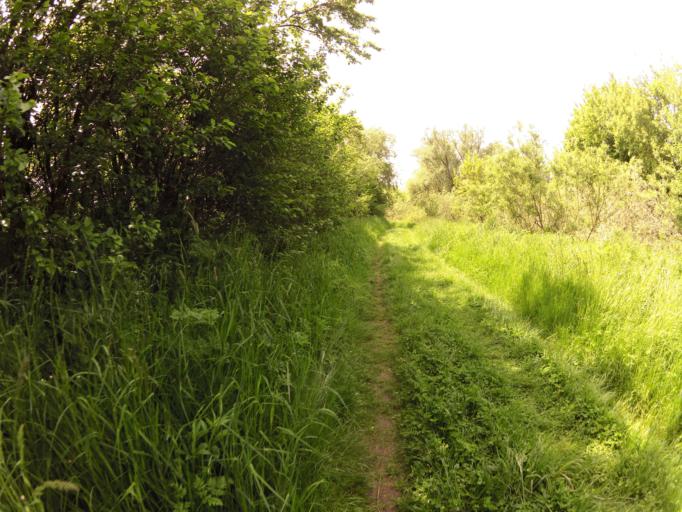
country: DE
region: Bavaria
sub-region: Regierungsbezirk Unterfranken
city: Nordheim
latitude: 49.8626
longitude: 10.1802
